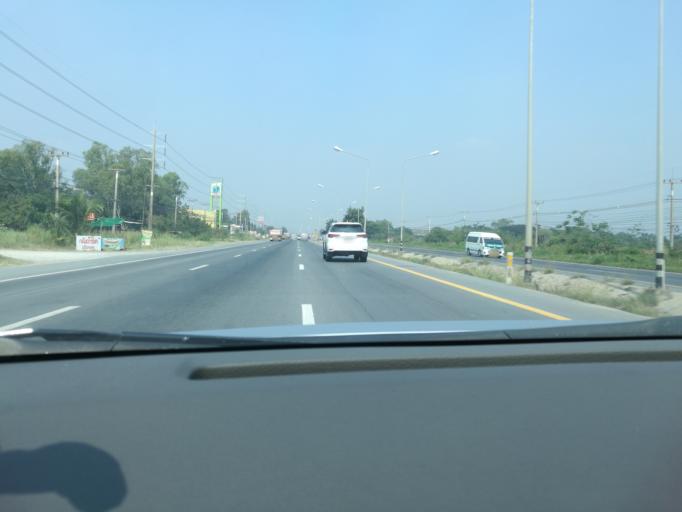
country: TH
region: Sara Buri
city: Chaloem Phra Kiat
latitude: 14.5944
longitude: 100.8974
